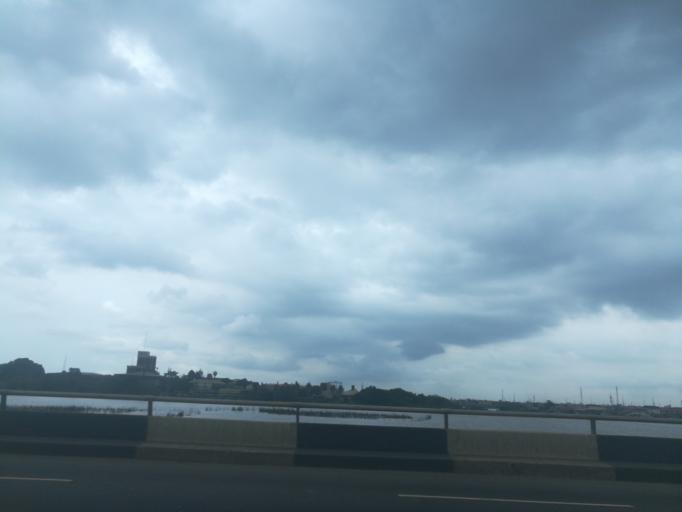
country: NG
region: Lagos
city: Makoko
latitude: 6.5235
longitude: 3.4041
